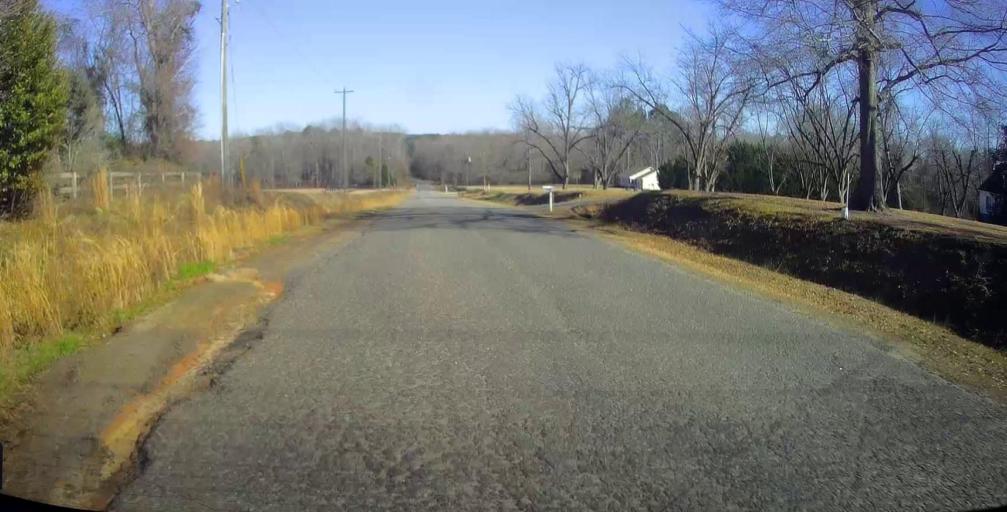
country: US
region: Georgia
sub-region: Crawford County
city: Roberta
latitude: 32.7156
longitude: -84.0056
